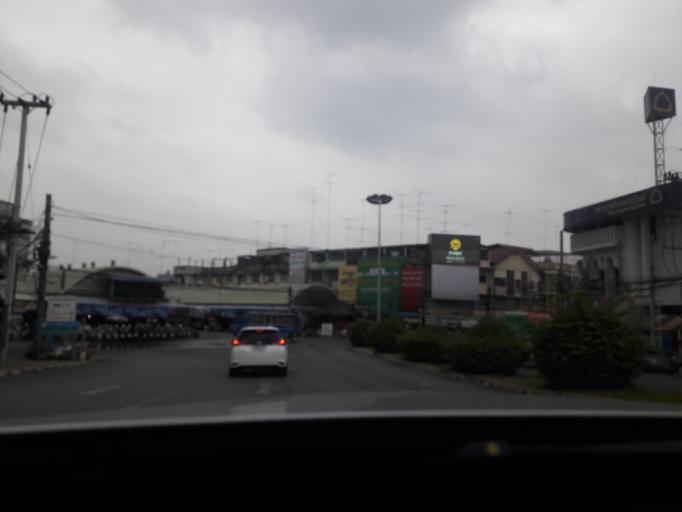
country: TH
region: Samut Songkhram
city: Samut Songkhram
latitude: 13.4060
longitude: 100.0007
